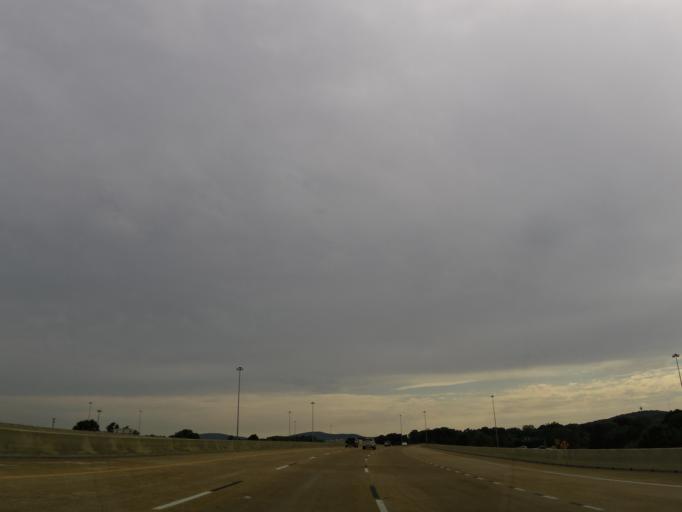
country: US
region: Alabama
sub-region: Madison County
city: Huntsville
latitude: 34.7348
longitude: -86.5952
